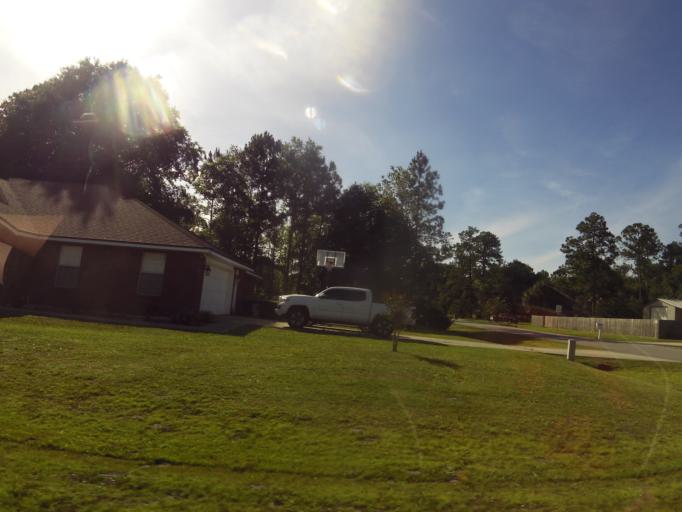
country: US
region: Florida
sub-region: Nassau County
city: Callahan
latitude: 30.5597
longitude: -81.7853
